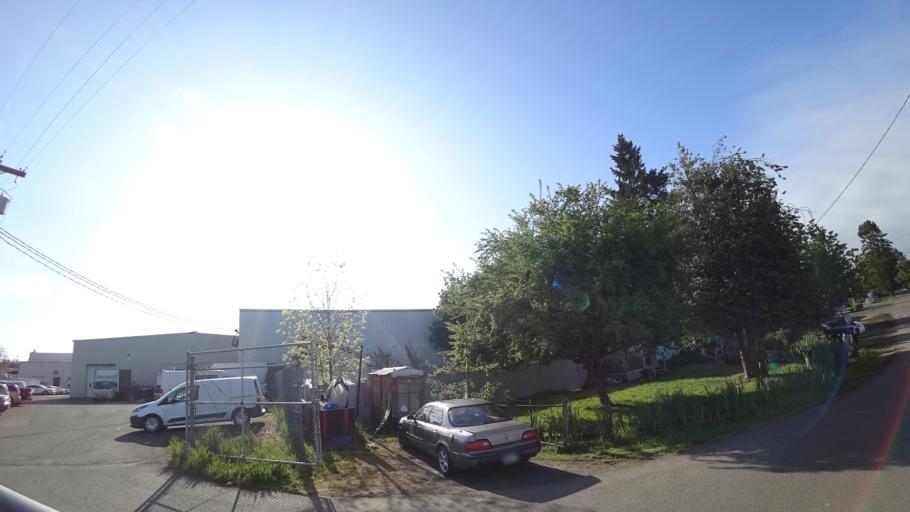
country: US
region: Oregon
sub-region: Washington County
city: Hillsboro
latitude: 45.5150
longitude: -122.9925
